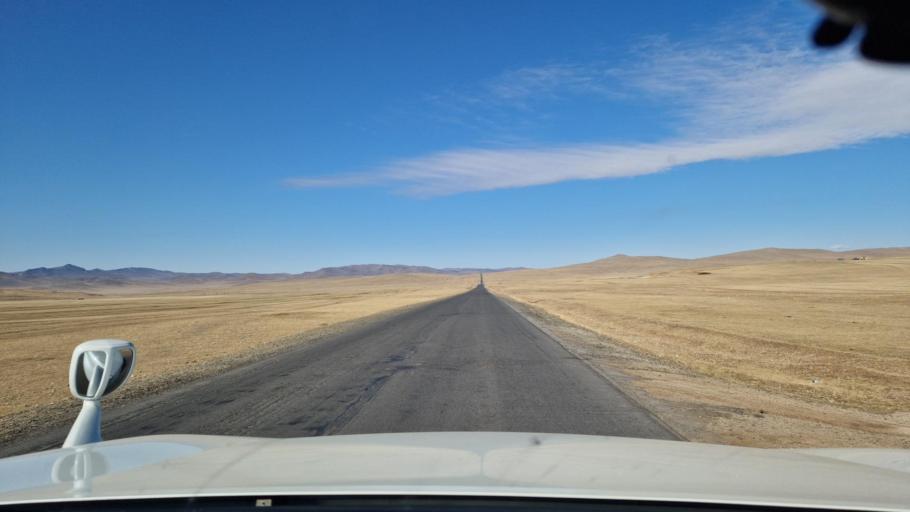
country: MN
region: Hentiy
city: Modot
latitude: 47.5967
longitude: 109.2476
